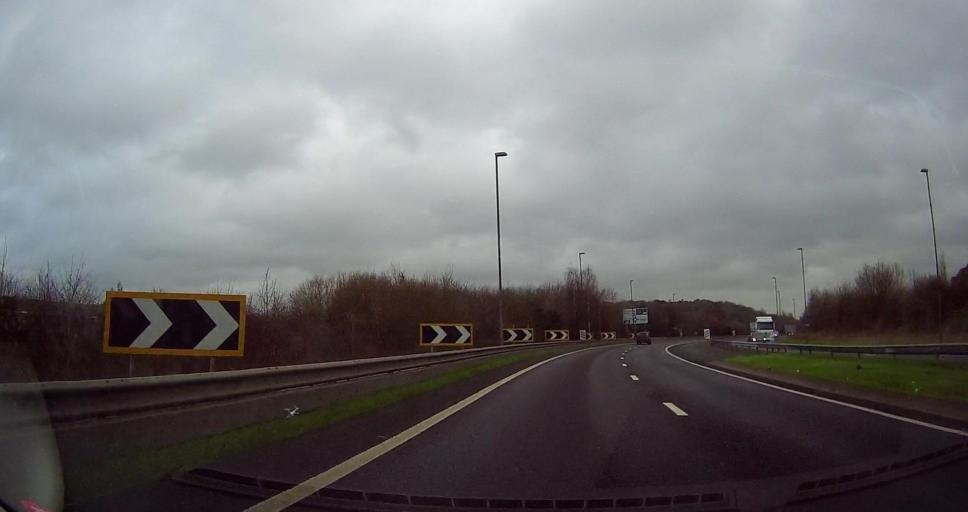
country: GB
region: England
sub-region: Kent
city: Strood
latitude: 51.4157
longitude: 0.5115
